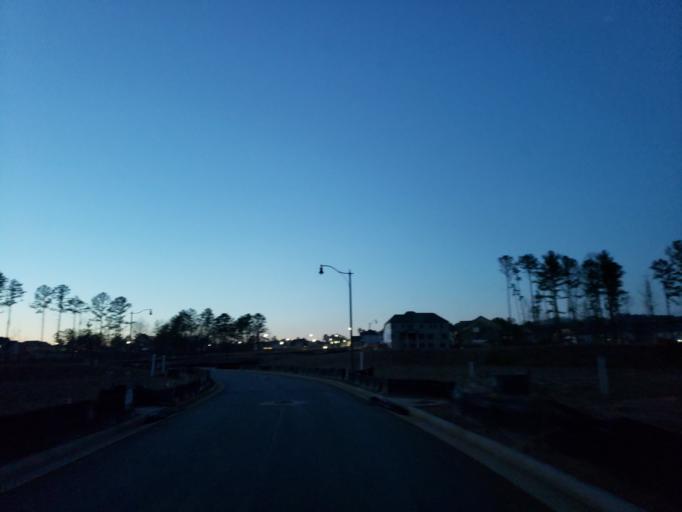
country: US
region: Georgia
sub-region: Cobb County
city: Powder Springs
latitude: 33.9320
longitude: -84.6944
